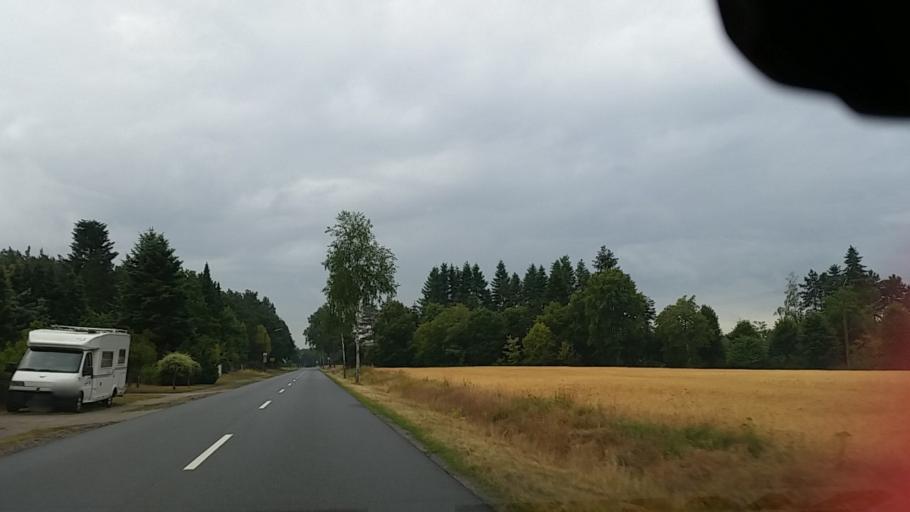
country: DE
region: Lower Saxony
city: Schoneworde
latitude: 52.6202
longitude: 10.6886
